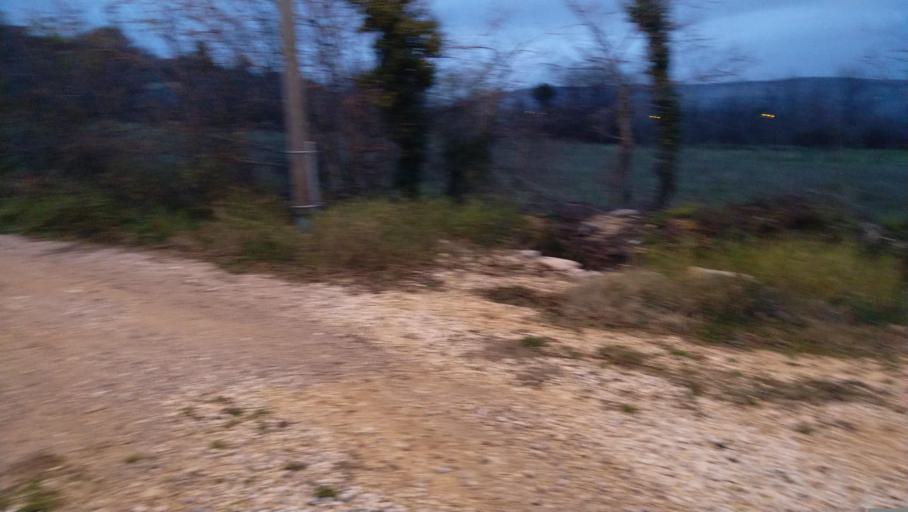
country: HR
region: Sibensko-Kniniska
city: Drnis
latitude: 43.8814
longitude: 16.2024
